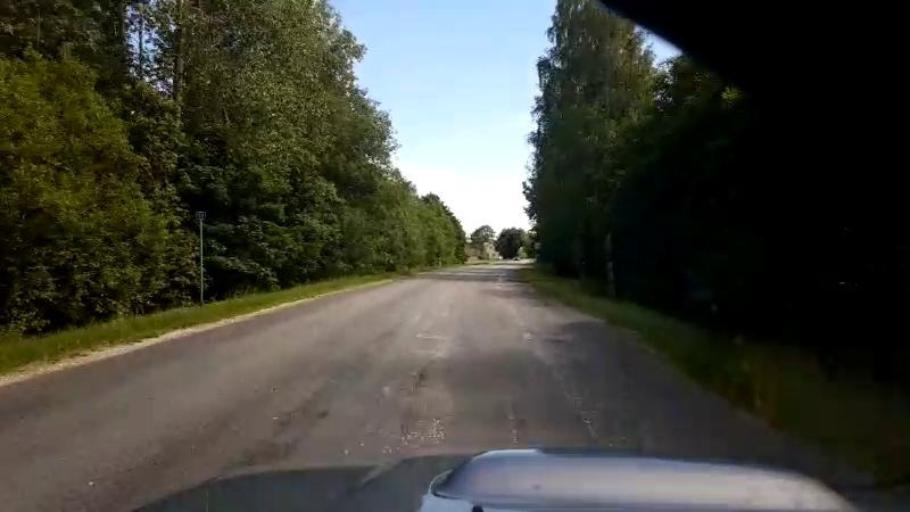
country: EE
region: Laeaene-Virumaa
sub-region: Rakke vald
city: Rakke
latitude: 58.9123
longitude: 26.2724
